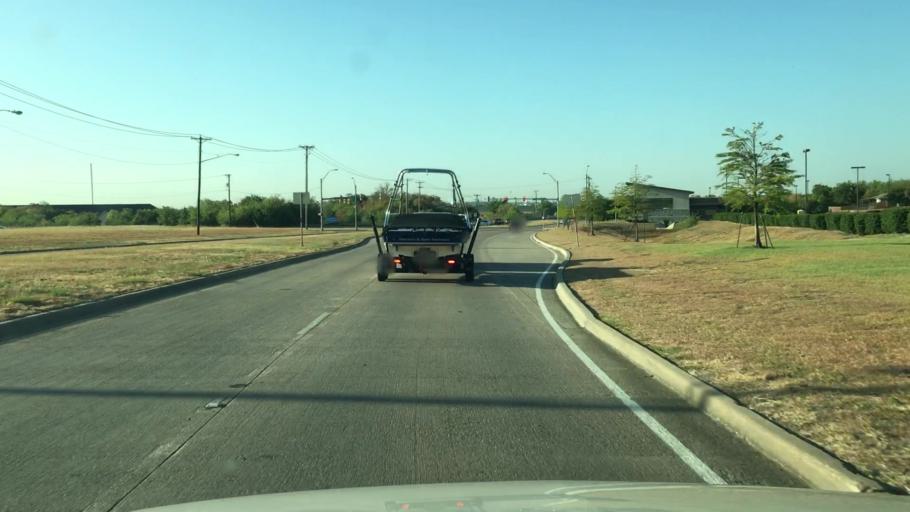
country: US
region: Texas
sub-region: Johnson County
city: Burleson
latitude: 32.5316
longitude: -97.3533
